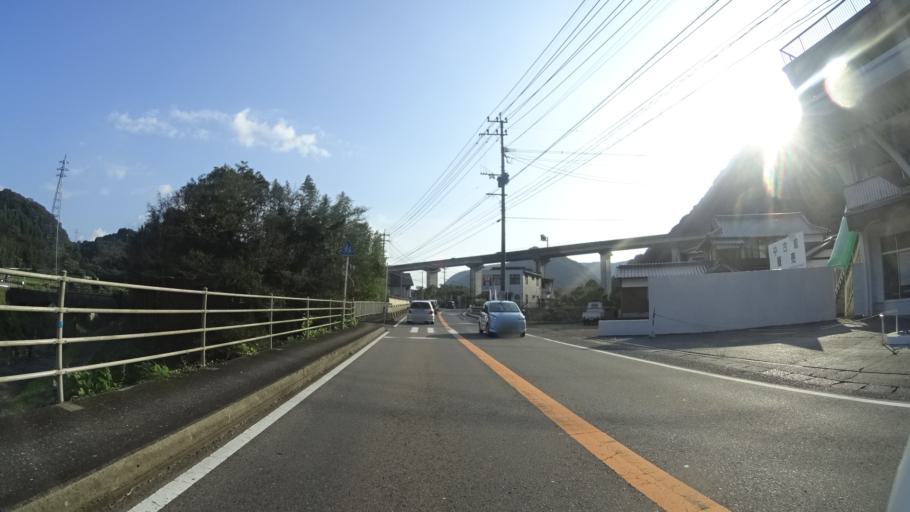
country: JP
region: Oita
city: Bungo-Takada-shi
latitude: 33.4796
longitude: 131.3343
